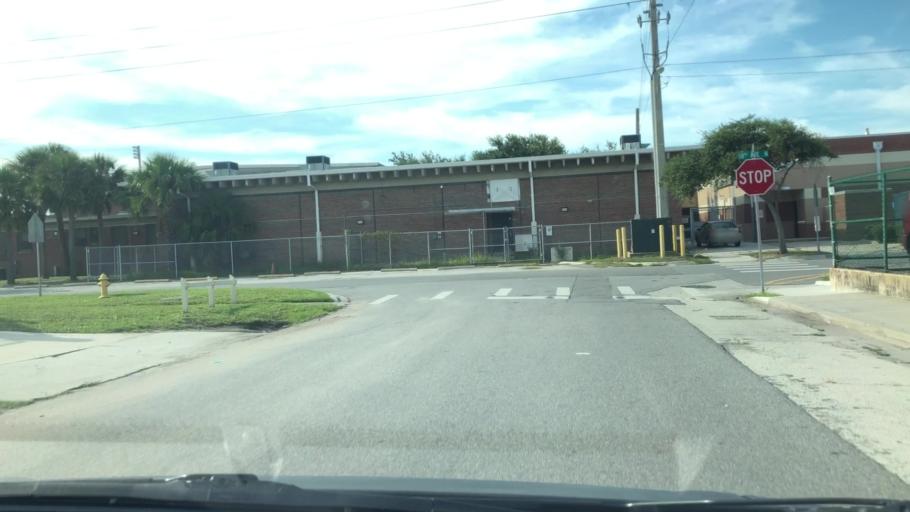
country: US
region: Florida
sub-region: Duval County
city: Neptune Beach
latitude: 30.3054
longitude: -81.3965
